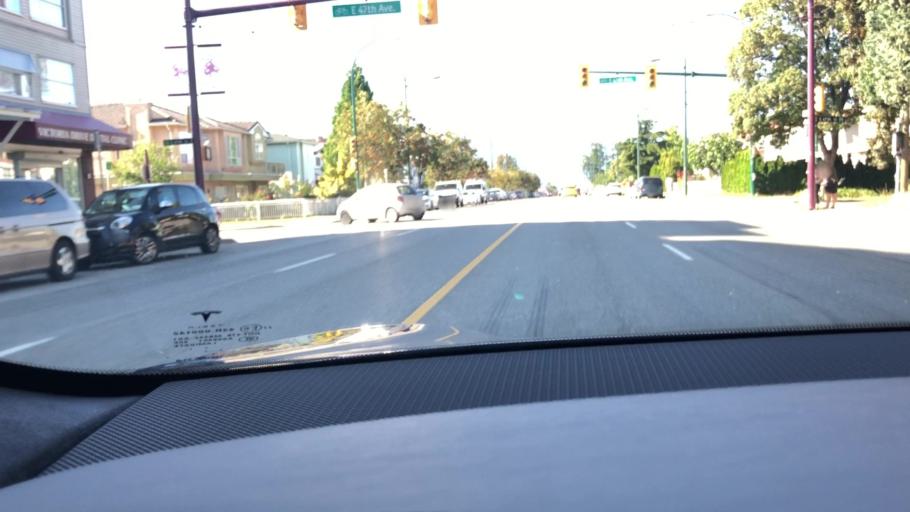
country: CA
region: British Columbia
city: Vancouver
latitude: 49.2272
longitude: -123.0657
